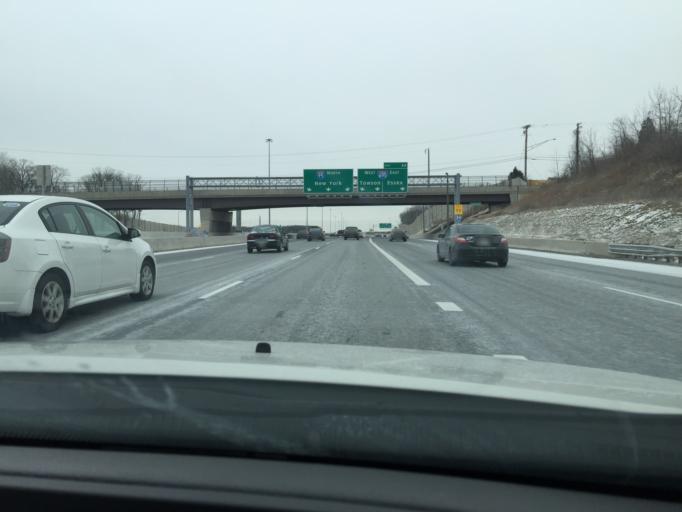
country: US
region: Maryland
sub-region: Baltimore County
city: Overlea
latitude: 39.3452
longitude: -76.5082
